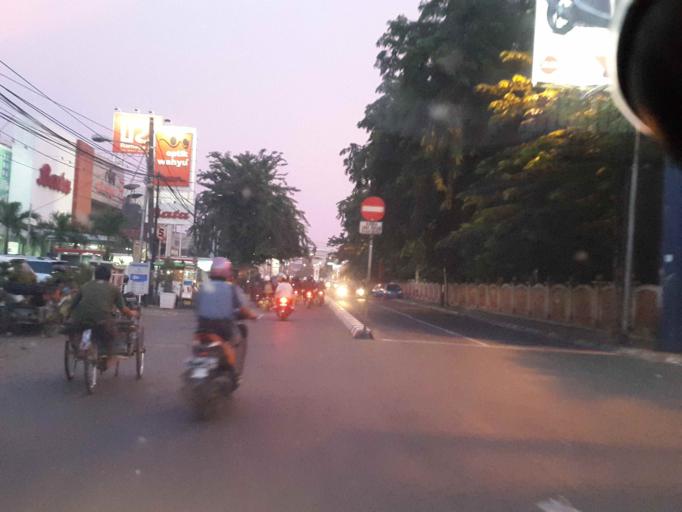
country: ID
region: West Java
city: Bekasi
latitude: -6.2471
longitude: 107.0103
